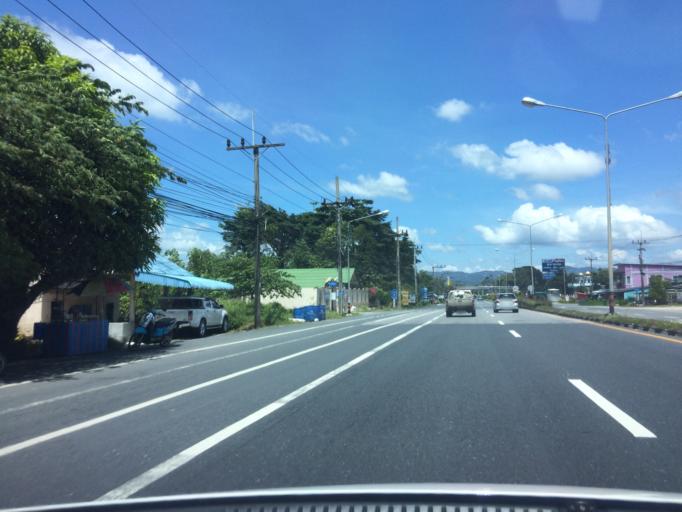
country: TH
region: Phangnga
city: Thai Mueang
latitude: 8.2187
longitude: 98.2976
